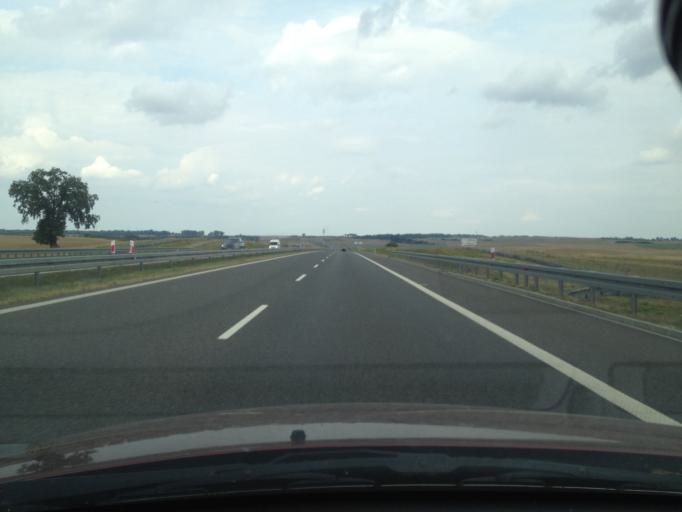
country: PL
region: West Pomeranian Voivodeship
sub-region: Powiat pyrzycki
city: Kozielice
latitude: 53.0313
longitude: 14.8639
